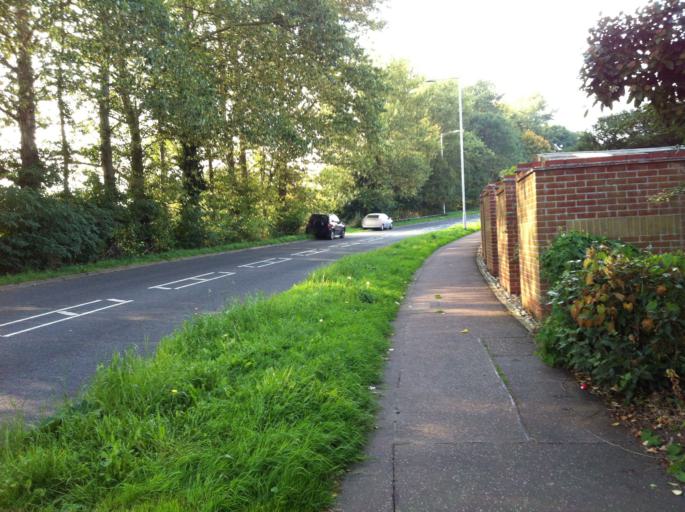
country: GB
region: England
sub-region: Norfolk
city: Bowthorpe
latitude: 52.6379
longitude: 1.2101
